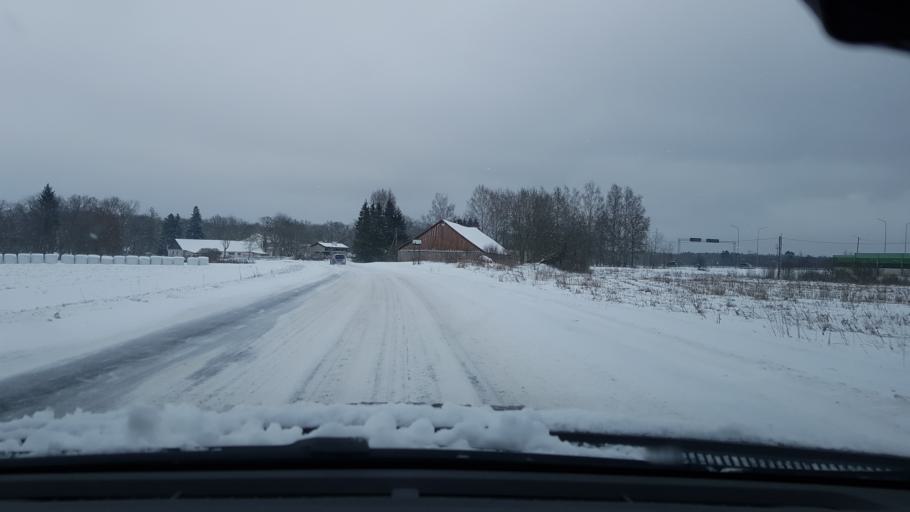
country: EE
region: Harju
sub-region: Kuusalu vald
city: Kuusalu
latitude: 59.4469
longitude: 25.3786
